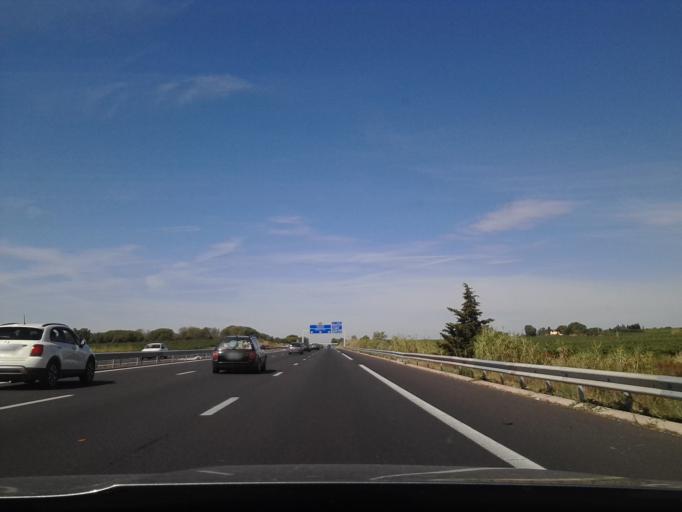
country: FR
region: Languedoc-Roussillon
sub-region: Departement de l'Herault
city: Cers
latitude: 43.3439
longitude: 3.3162
